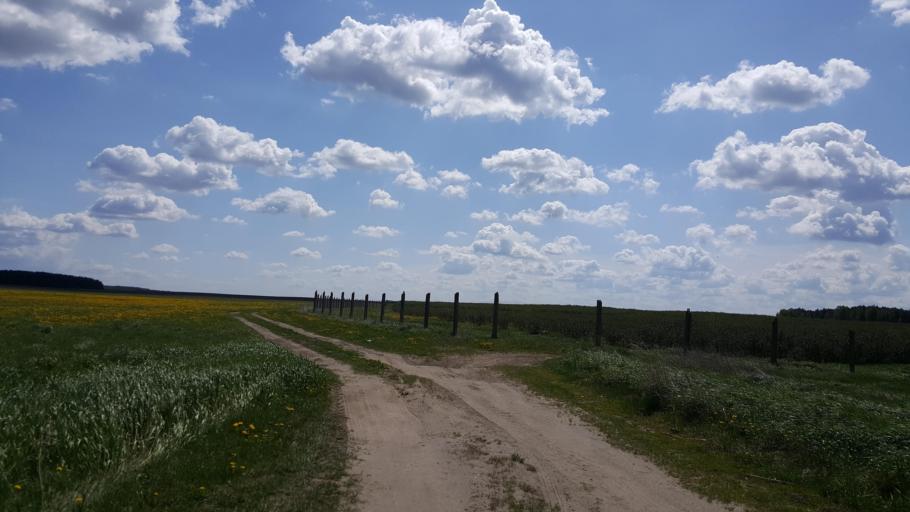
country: BY
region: Brest
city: Kamyanyets
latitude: 52.3878
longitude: 23.8908
